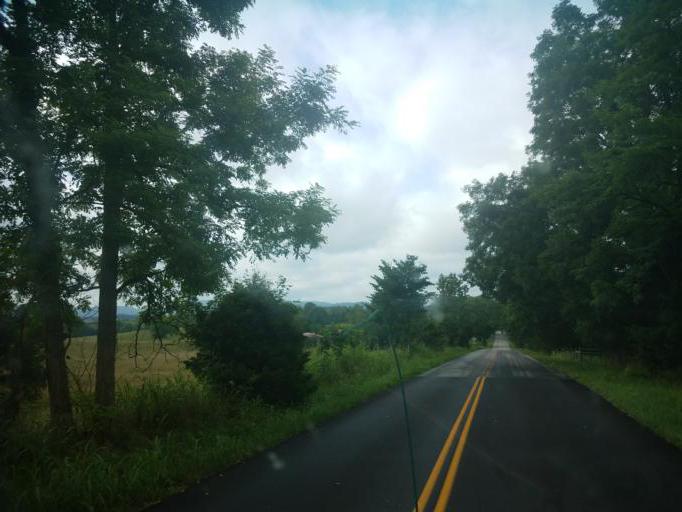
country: US
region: Kentucky
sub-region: Clinton County
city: Albany
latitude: 36.7779
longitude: -85.1415
